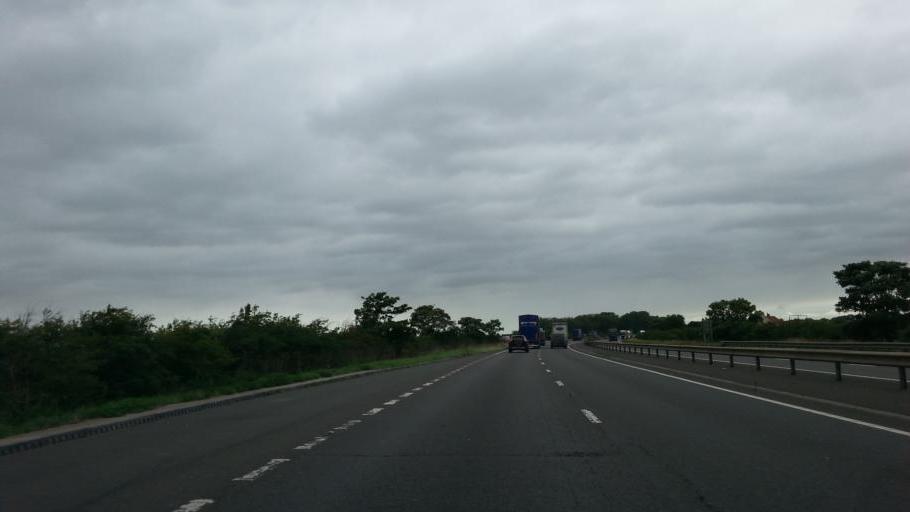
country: GB
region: England
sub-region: Nottinghamshire
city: Newark on Trent
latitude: 53.1116
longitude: -0.8143
